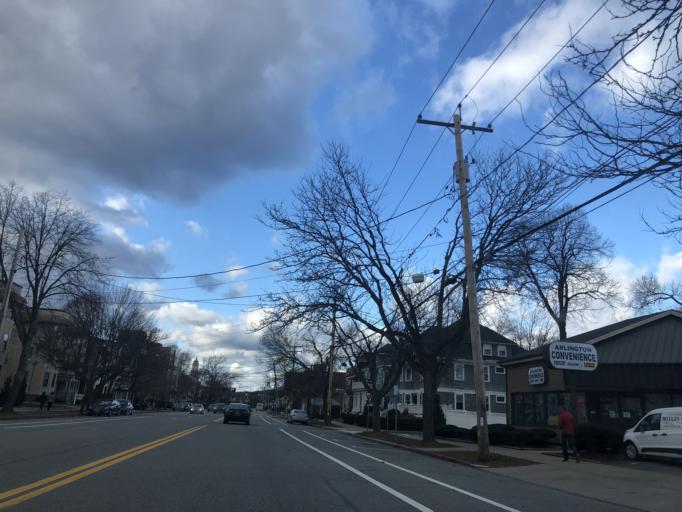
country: US
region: Massachusetts
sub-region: Middlesex County
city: Arlington
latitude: 42.4072
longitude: -71.1440
